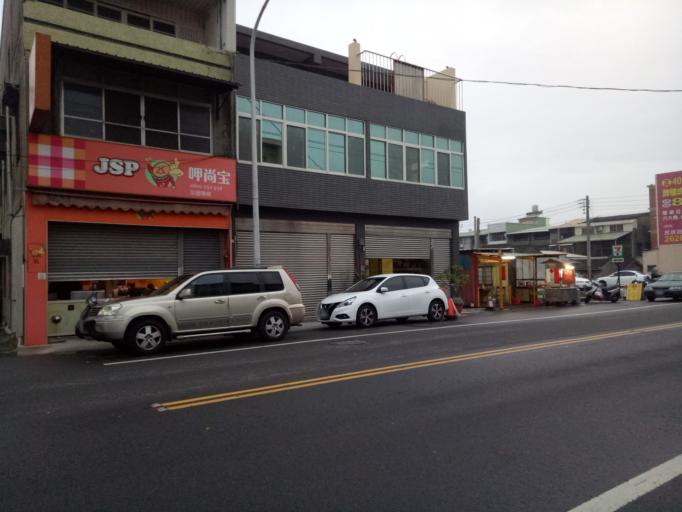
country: TW
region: Taiwan
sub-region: Changhua
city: Chang-hua
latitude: 24.2460
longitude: 120.5377
